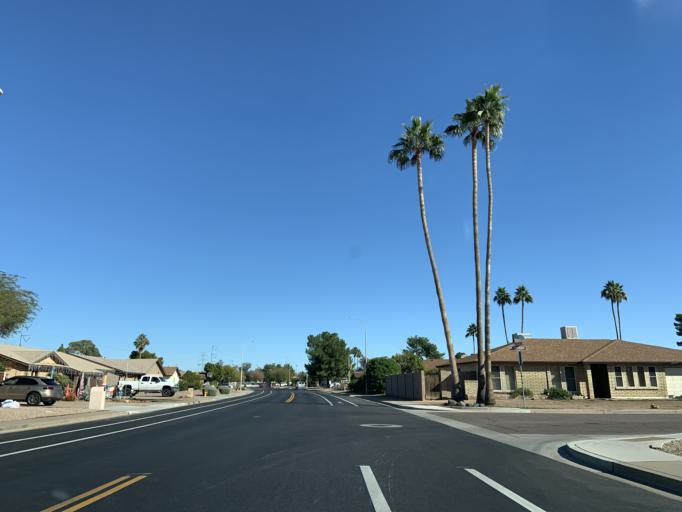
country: US
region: Arizona
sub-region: Maricopa County
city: San Carlos
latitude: 33.3540
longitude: -111.8739
